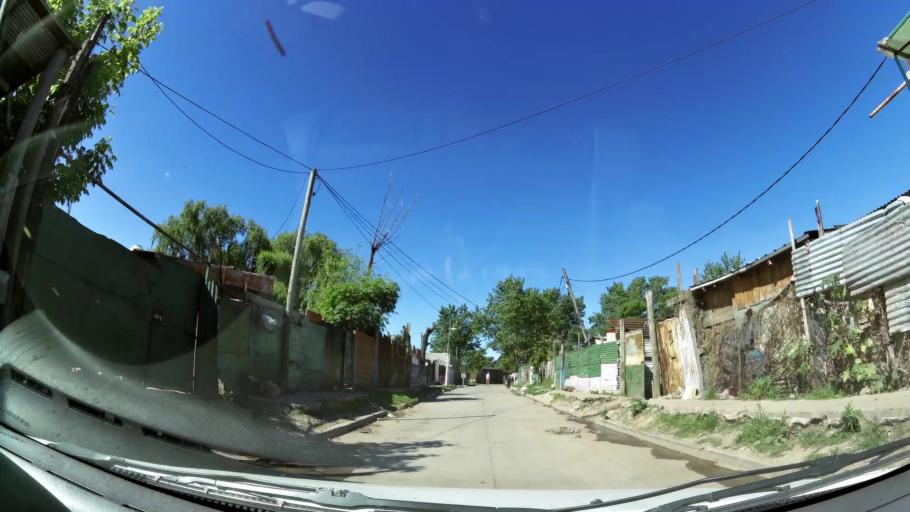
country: AR
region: Buenos Aires
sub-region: Partido de Tigre
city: Tigre
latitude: -34.5072
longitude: -58.5876
